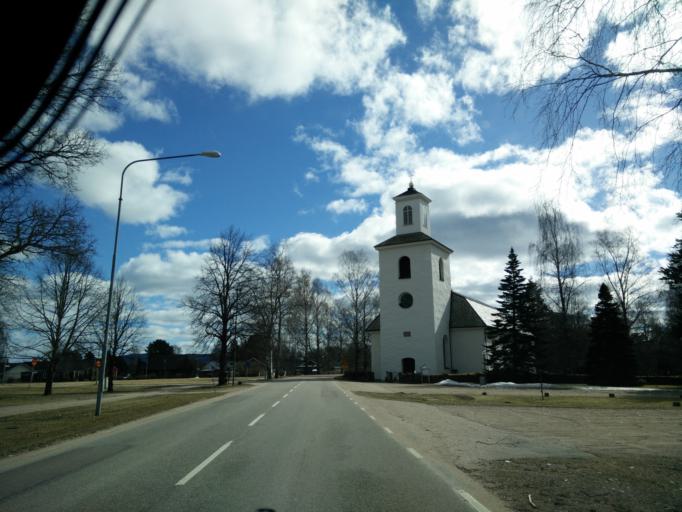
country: SE
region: Vaermland
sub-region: Hagfors Kommun
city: Hagfors
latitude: 60.0049
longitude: 13.5972
